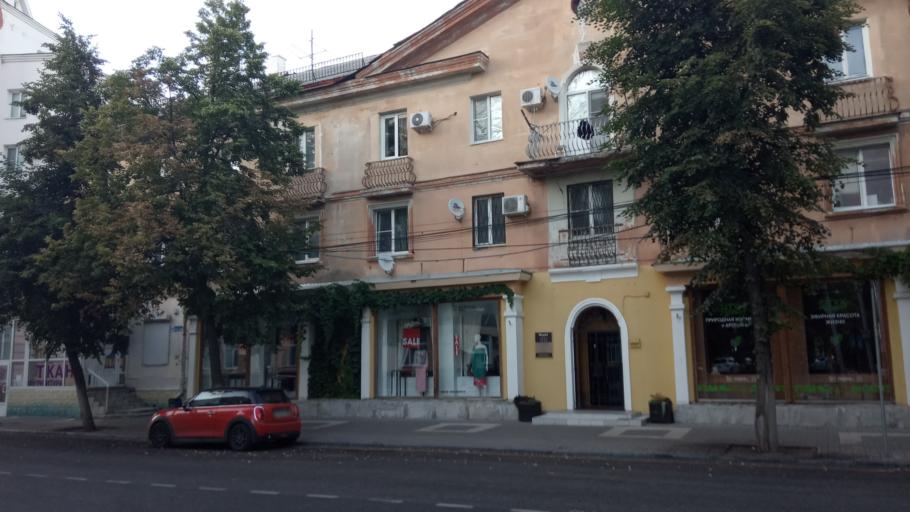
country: RU
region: Voronezj
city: Voronezh
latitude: 51.6618
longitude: 39.2070
